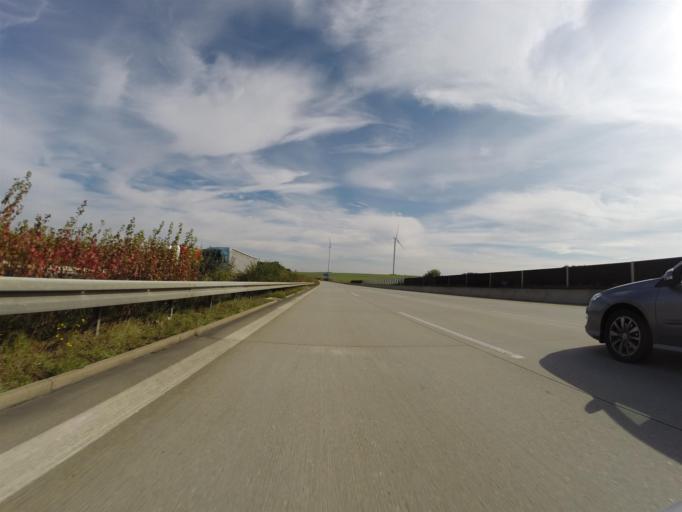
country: DE
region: Saxony
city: Dennheritz
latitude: 50.8265
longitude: 12.4711
